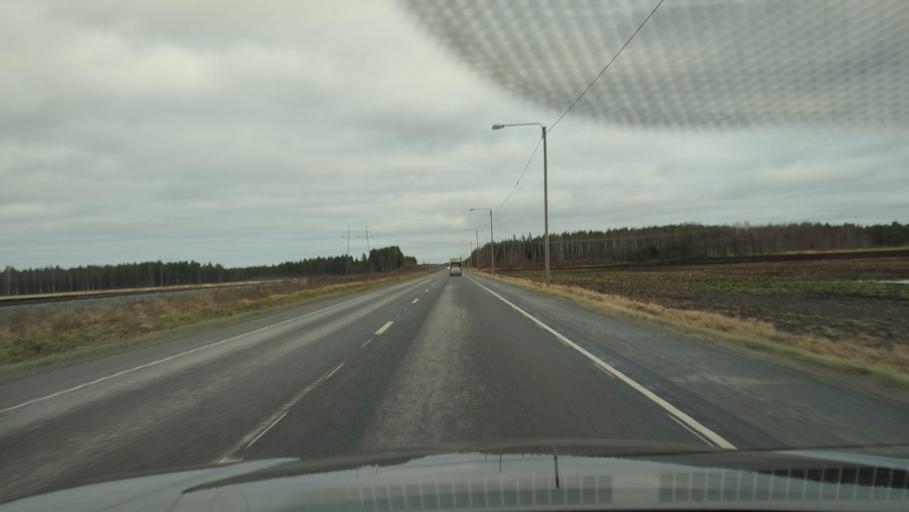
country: FI
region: Southern Ostrobothnia
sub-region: Seinaejoki
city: Ilmajoki
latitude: 62.7443
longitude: 22.6287
